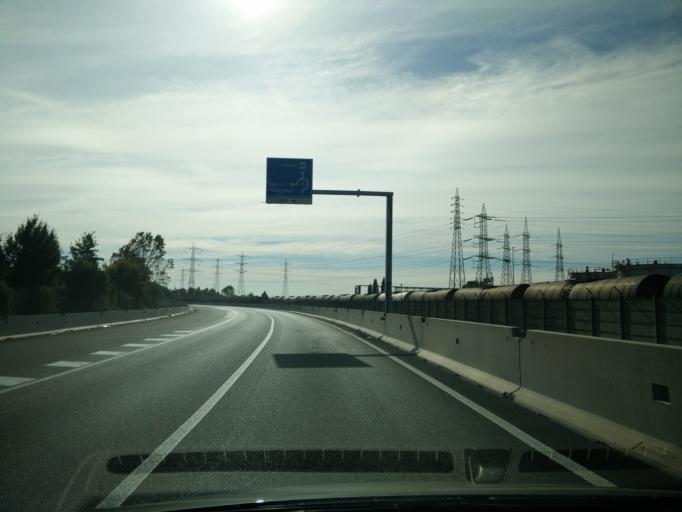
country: IT
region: Veneto
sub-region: Provincia di Venezia
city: Mestre
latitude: 45.4398
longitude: 12.2106
